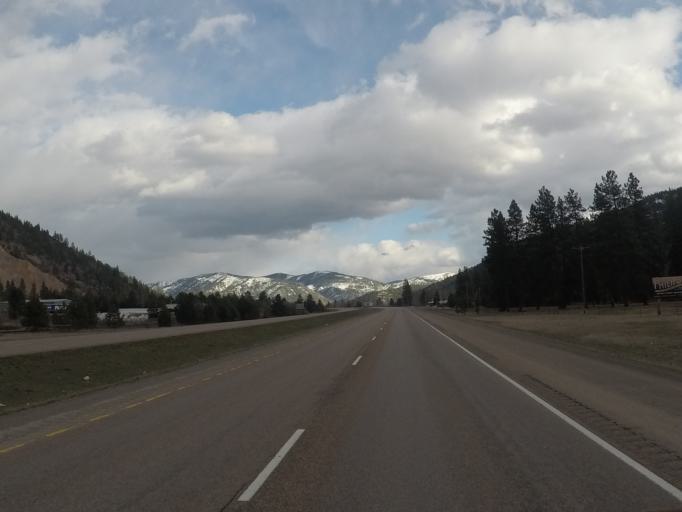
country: US
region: Montana
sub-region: Missoula County
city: Clinton
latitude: 46.8026
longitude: -113.7737
